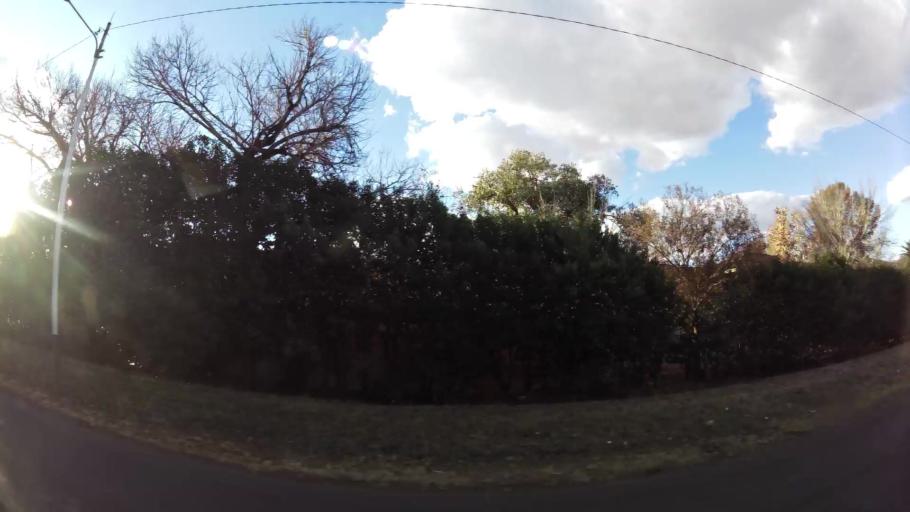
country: ZA
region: North-West
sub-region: Dr Kenneth Kaunda District Municipality
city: Potchefstroom
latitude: -26.7067
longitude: 27.0886
